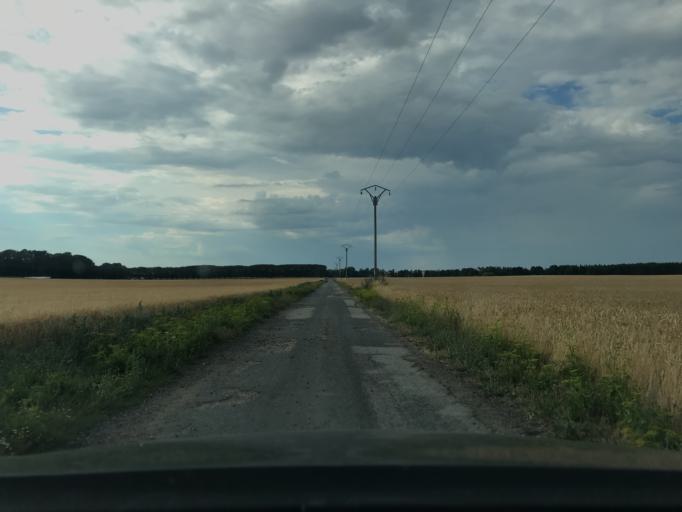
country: SE
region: Skane
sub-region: Simrishamns Kommun
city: Kivik
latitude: 55.5335
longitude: 14.1572
